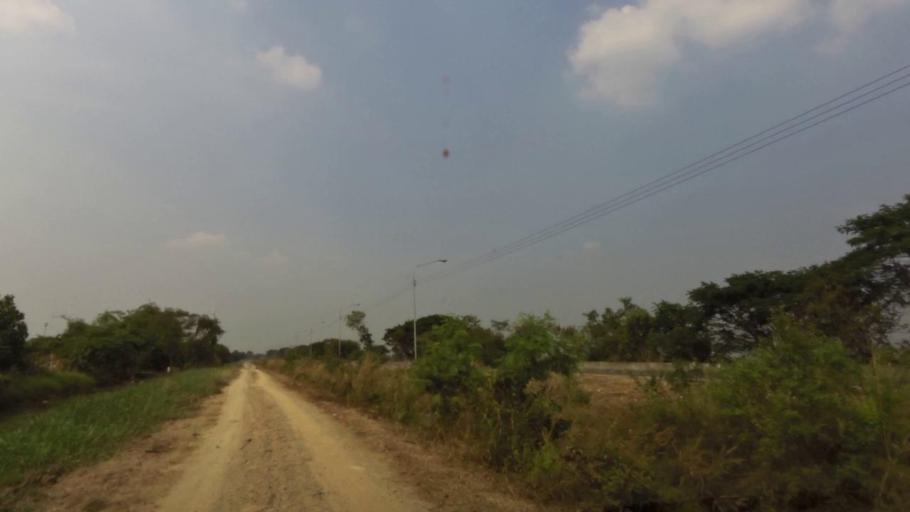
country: TH
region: Phra Nakhon Si Ayutthaya
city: Phra Nakhon Si Ayutthaya
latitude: 14.3176
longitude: 100.5609
